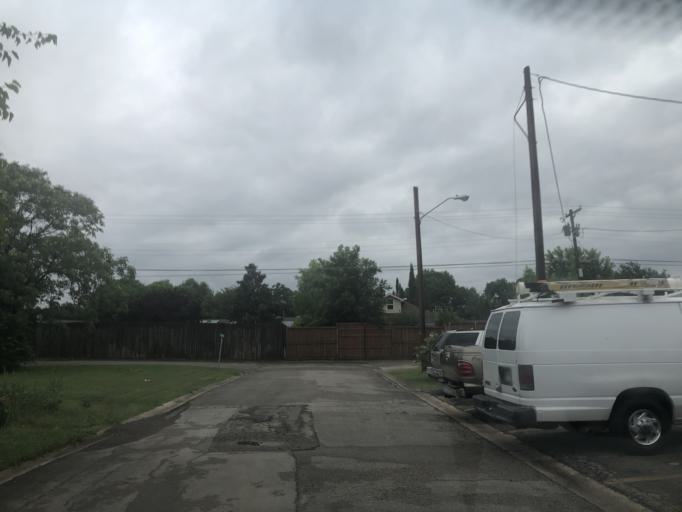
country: US
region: Texas
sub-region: Dallas County
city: Irving
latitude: 32.7846
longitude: -96.9695
